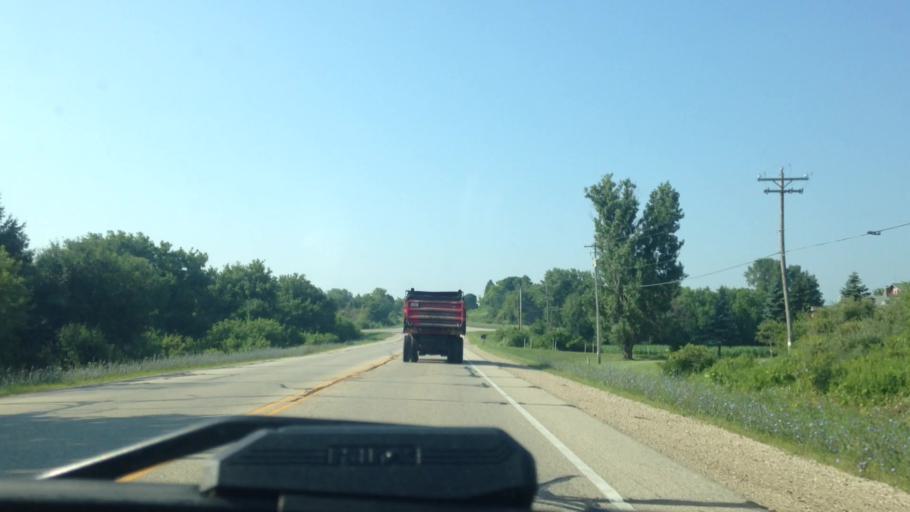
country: US
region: Wisconsin
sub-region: Waukesha County
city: Merton
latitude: 43.1684
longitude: -88.2625
